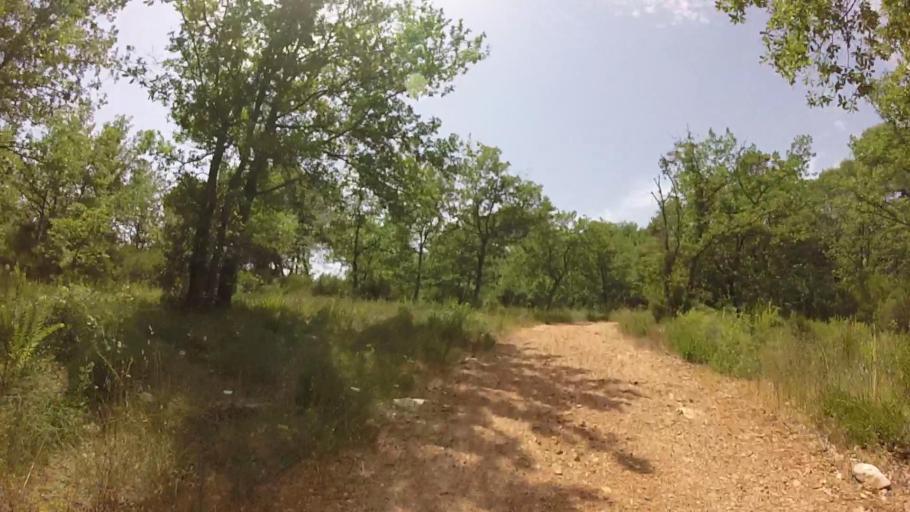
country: FR
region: Provence-Alpes-Cote d'Azur
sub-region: Departement des Alpes-Maritimes
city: Mougins
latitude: 43.6167
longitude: 7.0341
